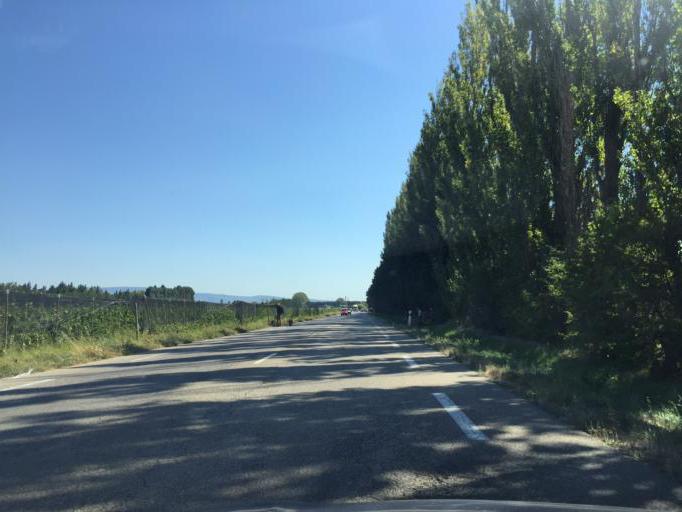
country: FR
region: Provence-Alpes-Cote d'Azur
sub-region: Departement du Vaucluse
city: Caumont-sur-Durance
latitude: 43.8844
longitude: 4.9791
